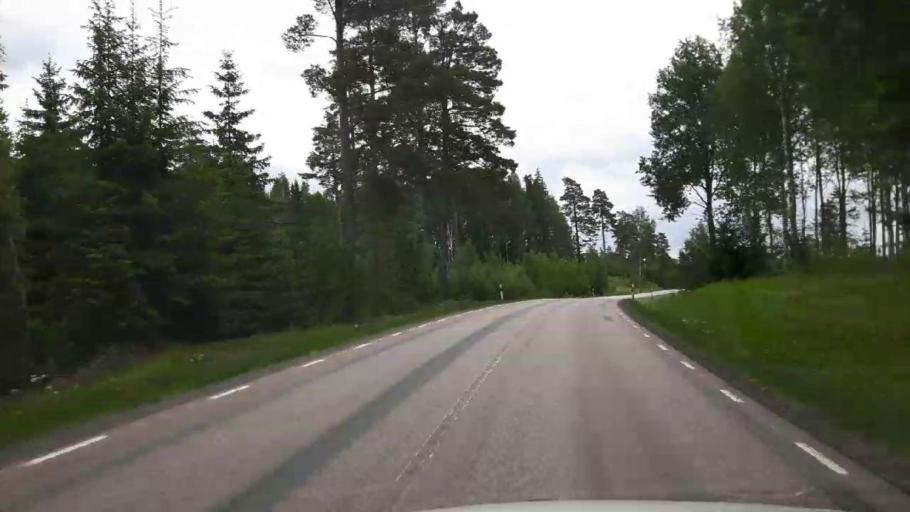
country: SE
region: Vaestmanland
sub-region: Kopings Kommun
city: Kolsva
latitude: 59.6408
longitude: 15.7949
